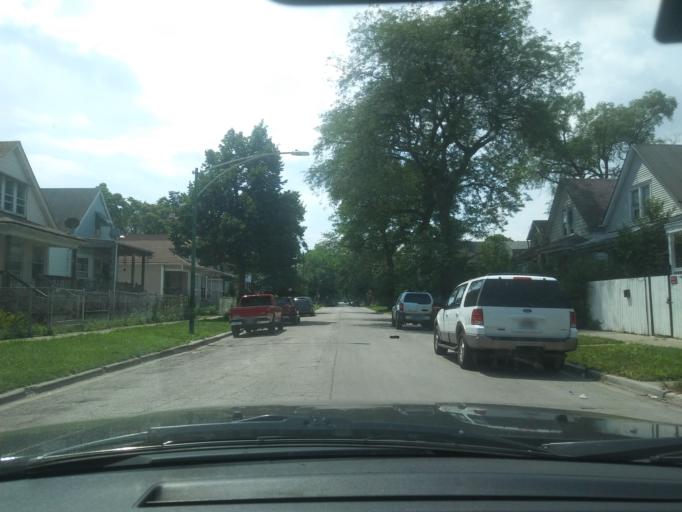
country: US
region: Illinois
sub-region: Cook County
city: Chicago
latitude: 41.7859
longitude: -87.6729
